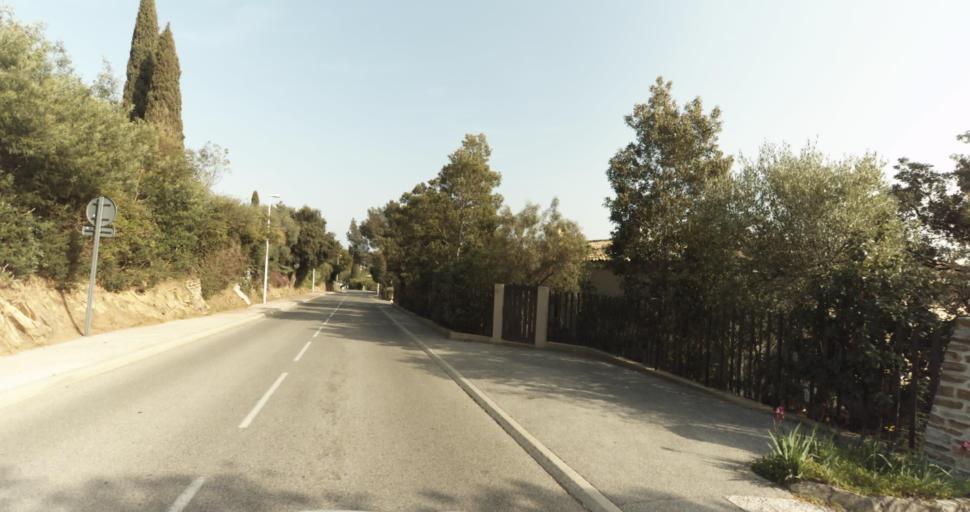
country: FR
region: Provence-Alpes-Cote d'Azur
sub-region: Departement du Var
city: Bormes-les-Mimosas
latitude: 43.1465
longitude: 6.3475
